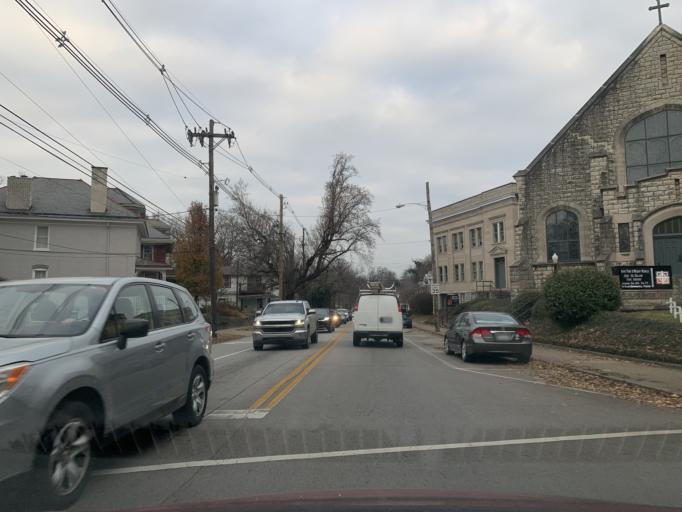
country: US
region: Kentucky
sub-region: Jefferson County
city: Audubon Park
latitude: 38.2392
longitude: -85.7195
